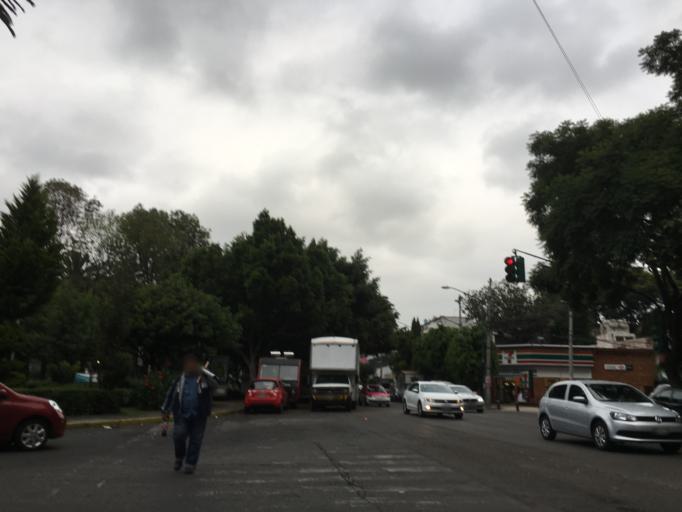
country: MX
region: Mexico City
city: Colonia del Valle
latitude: 19.3789
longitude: -99.1708
